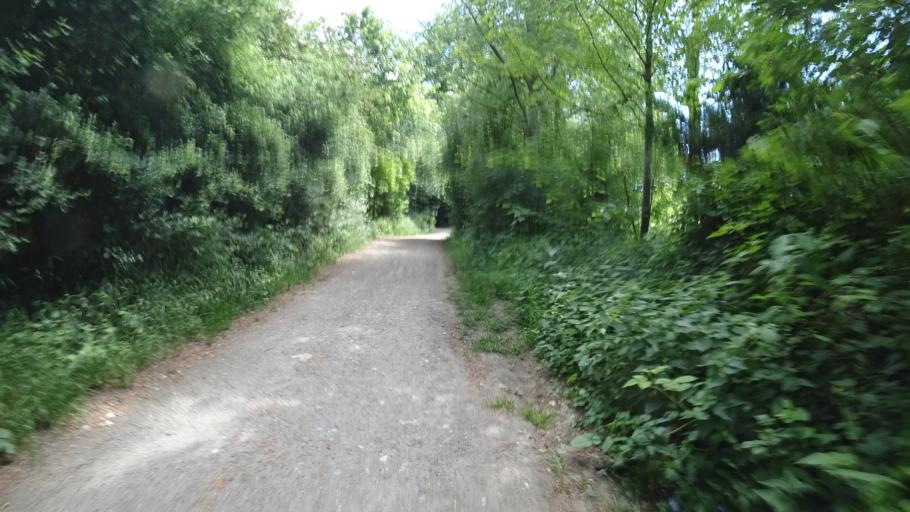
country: DE
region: North Rhine-Westphalia
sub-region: Regierungsbezirk Detmold
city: Rheda-Wiedenbruck
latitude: 51.8267
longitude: 8.3266
